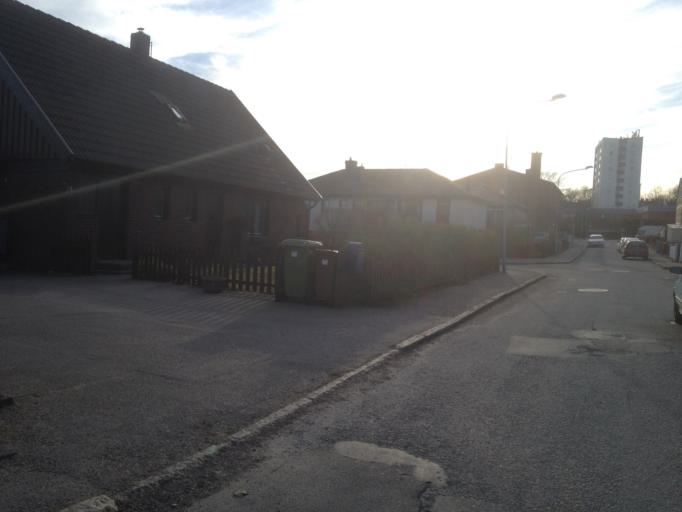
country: SE
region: OEstergoetland
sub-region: Norrkopings Kommun
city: Norrkoping
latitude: 58.6018
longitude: 16.1706
